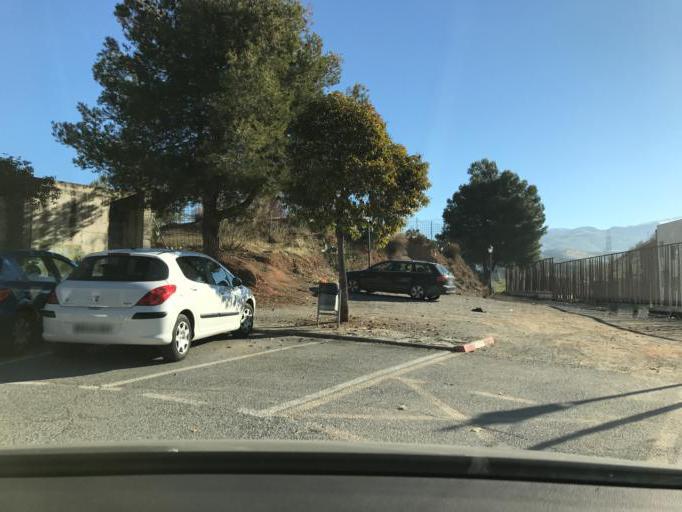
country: ES
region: Andalusia
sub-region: Provincia de Granada
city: Huetor Vega
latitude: 37.1611
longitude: -3.5766
